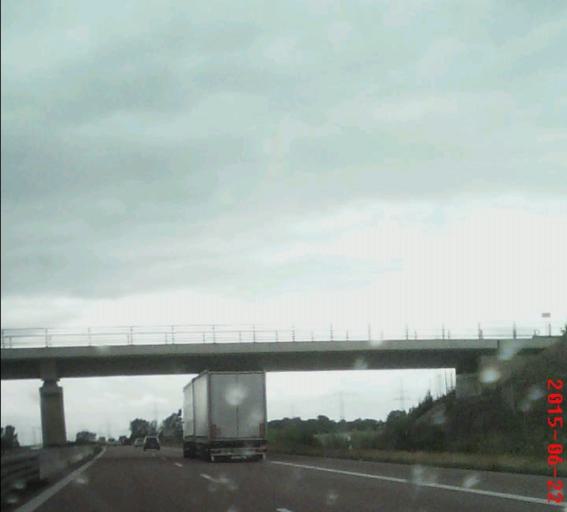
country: DE
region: Saxony-Anhalt
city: Bad Lauchstadt
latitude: 51.4052
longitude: 11.8291
